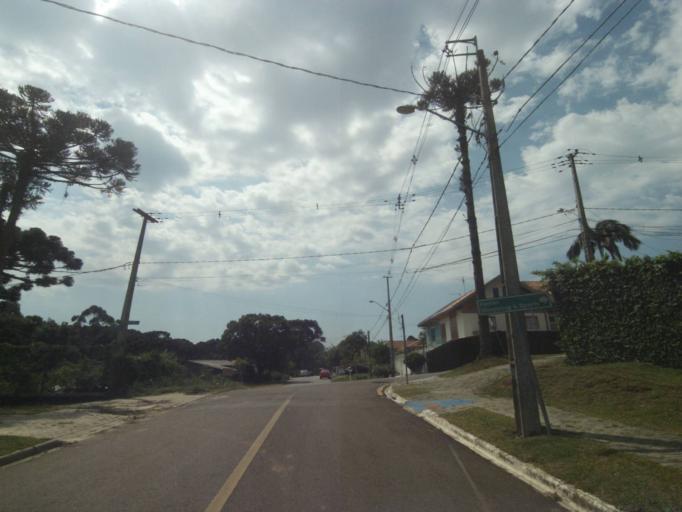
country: BR
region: Parana
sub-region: Sao Jose Dos Pinhais
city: Sao Jose dos Pinhais
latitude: -25.5187
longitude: -49.2581
